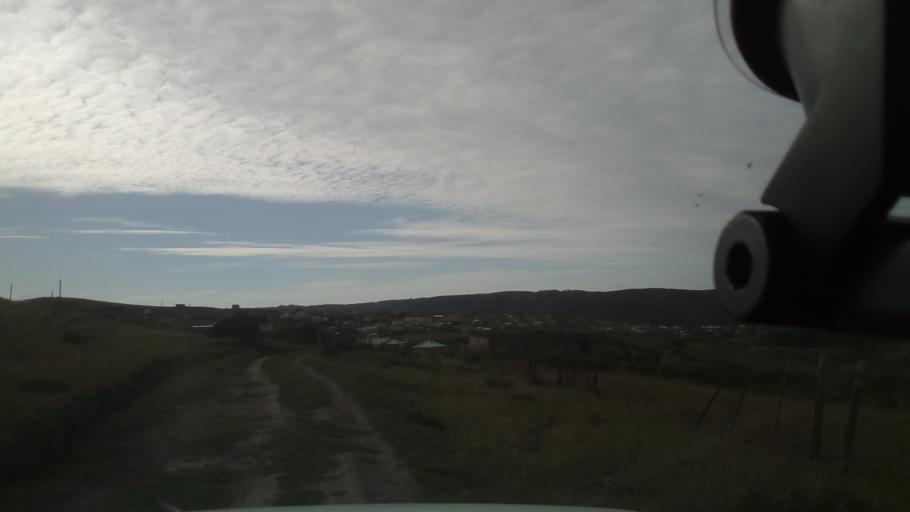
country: ZA
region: Eastern Cape
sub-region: Buffalo City Metropolitan Municipality
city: East London
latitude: -32.8011
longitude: 27.9646
